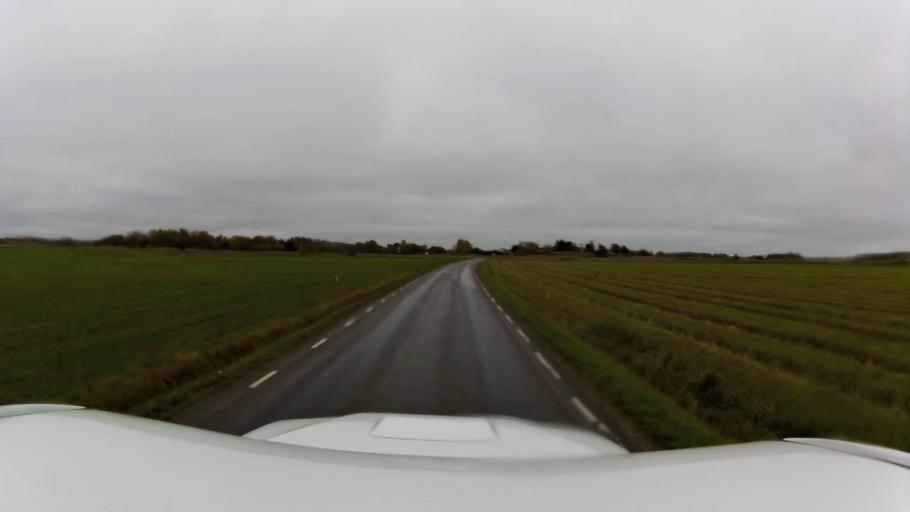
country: SE
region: OEstergoetland
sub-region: Linkopings Kommun
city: Ekangen
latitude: 58.4678
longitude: 15.6971
